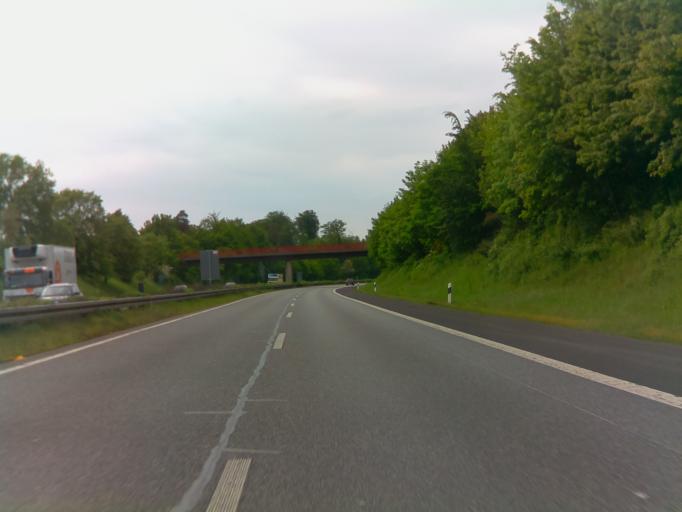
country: DE
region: Hesse
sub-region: Regierungsbezirk Giessen
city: Fronhausen
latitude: 50.7064
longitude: 8.7276
